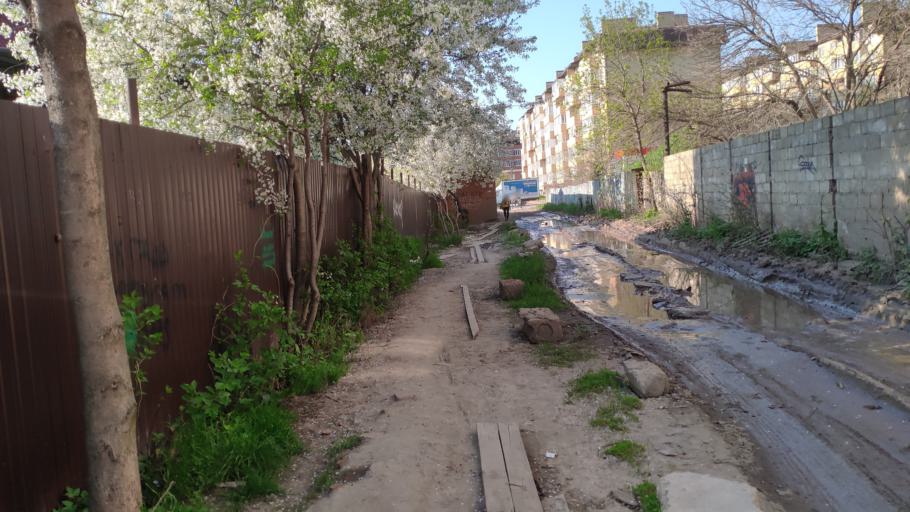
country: RU
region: Krasnodarskiy
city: Krasnodar
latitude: 45.0833
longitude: 39.0102
